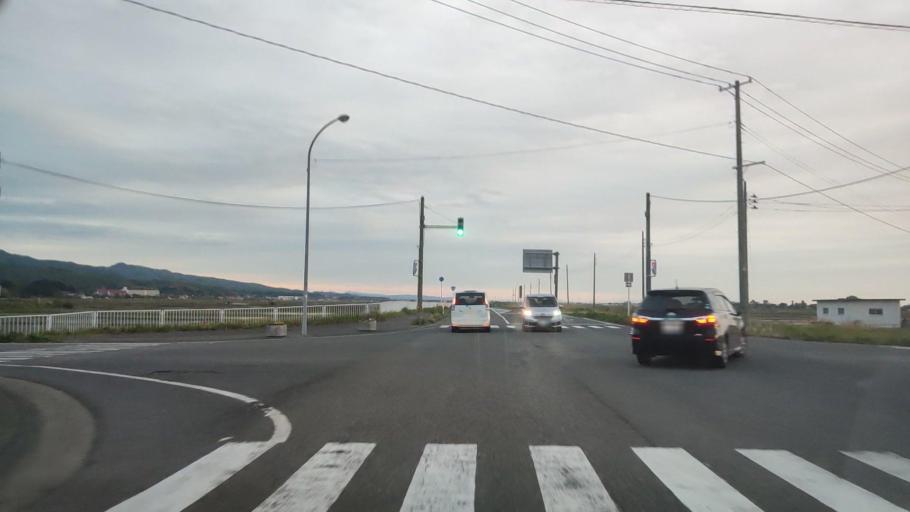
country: JP
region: Niigata
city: Niitsu-honcho
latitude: 37.7713
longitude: 139.1030
